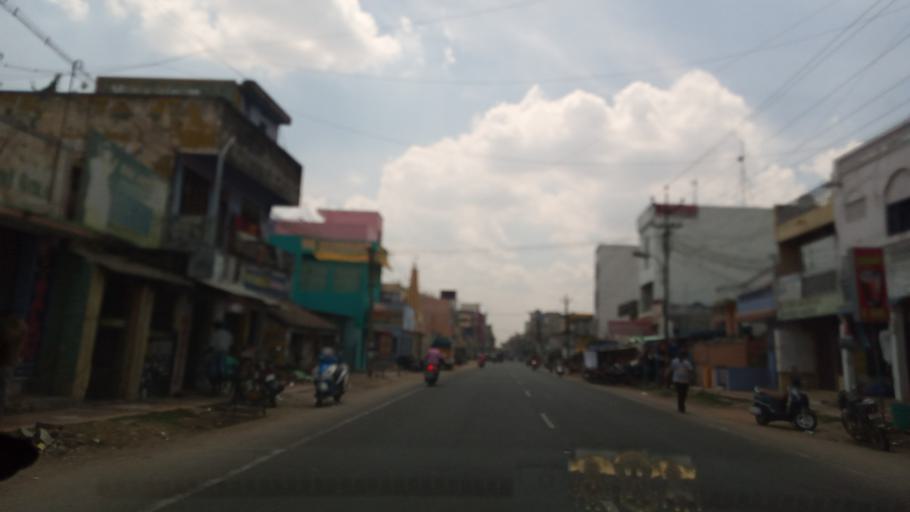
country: IN
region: Tamil Nadu
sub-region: Vellore
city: Walajapet
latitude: 12.9250
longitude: 79.3689
